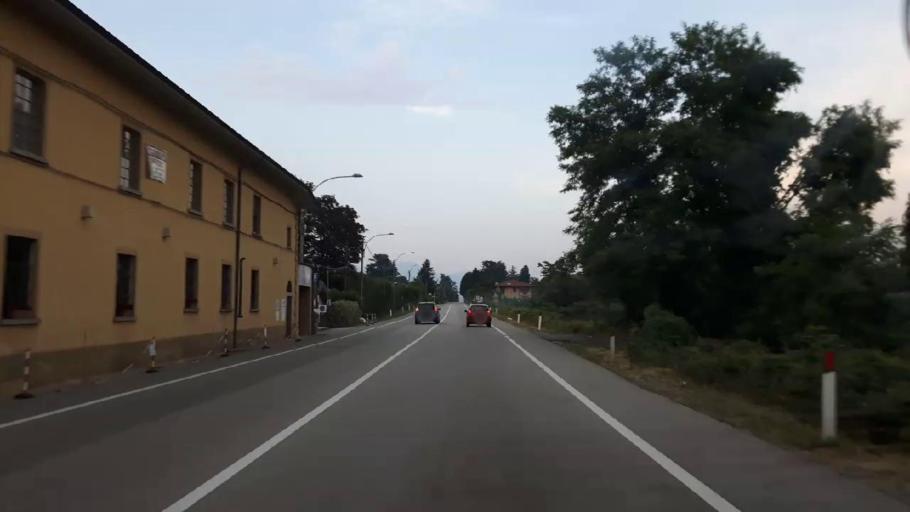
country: IT
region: Piedmont
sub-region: Provincia di Novara
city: Lesa
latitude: 45.8199
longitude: 8.5539
